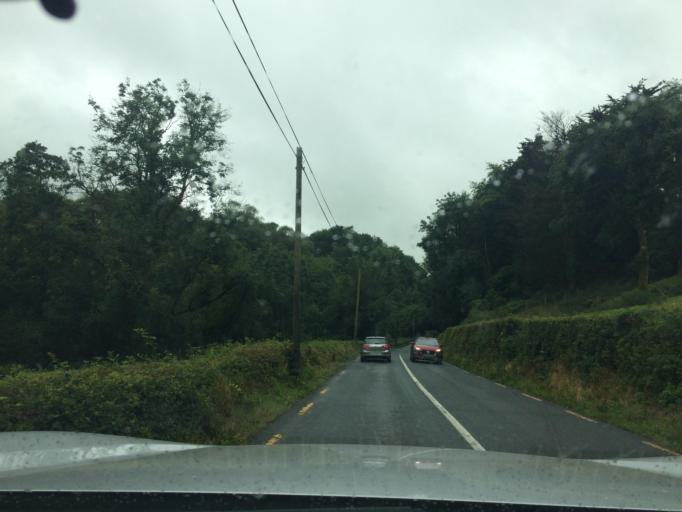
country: IE
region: Munster
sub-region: South Tipperary
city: Cluain Meala
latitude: 52.2627
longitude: -7.7098
